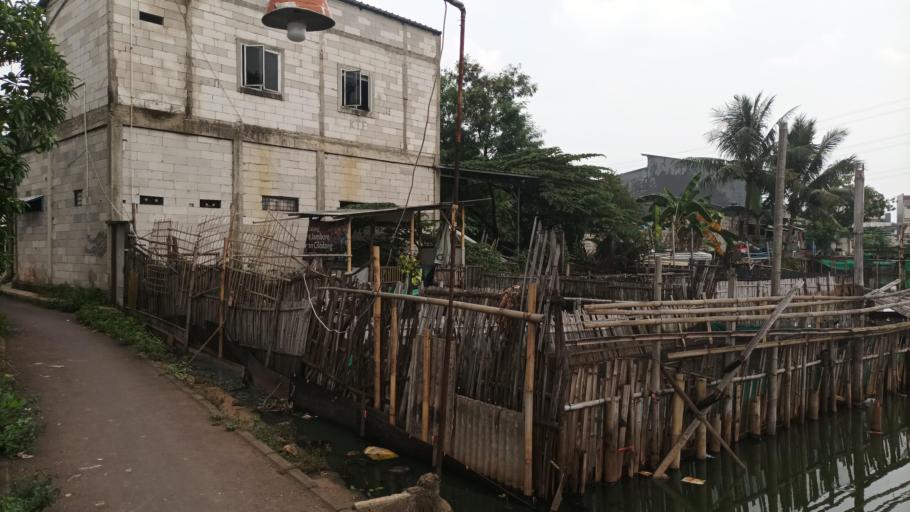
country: ID
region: West Java
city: Depok
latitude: -6.4233
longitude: 106.8523
